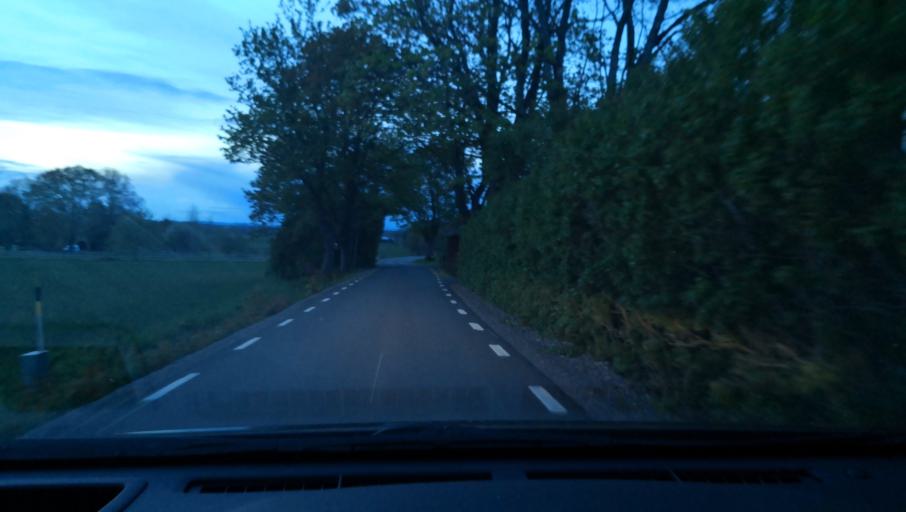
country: SE
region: OErebro
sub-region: Askersunds Kommun
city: Asbro
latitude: 59.0539
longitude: 14.9310
